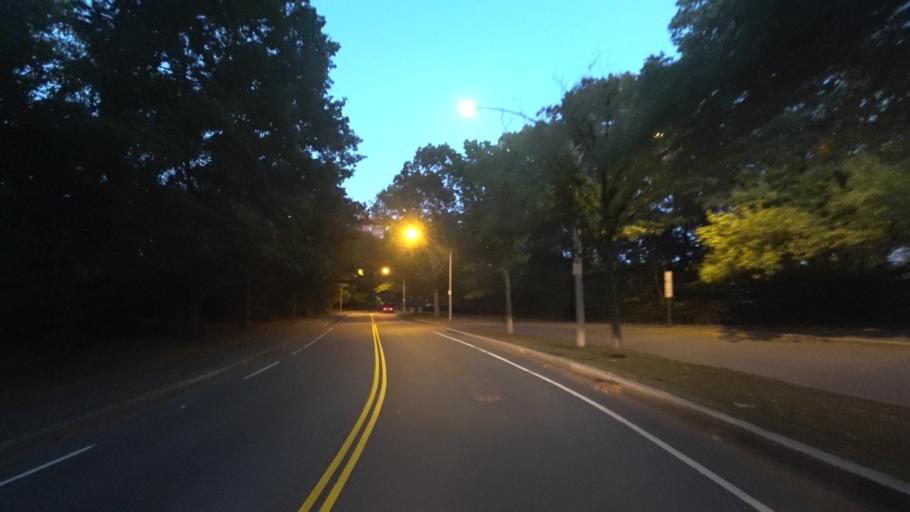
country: US
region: Massachusetts
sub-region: Norfolk County
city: Brookline
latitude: 42.3378
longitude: -71.1596
